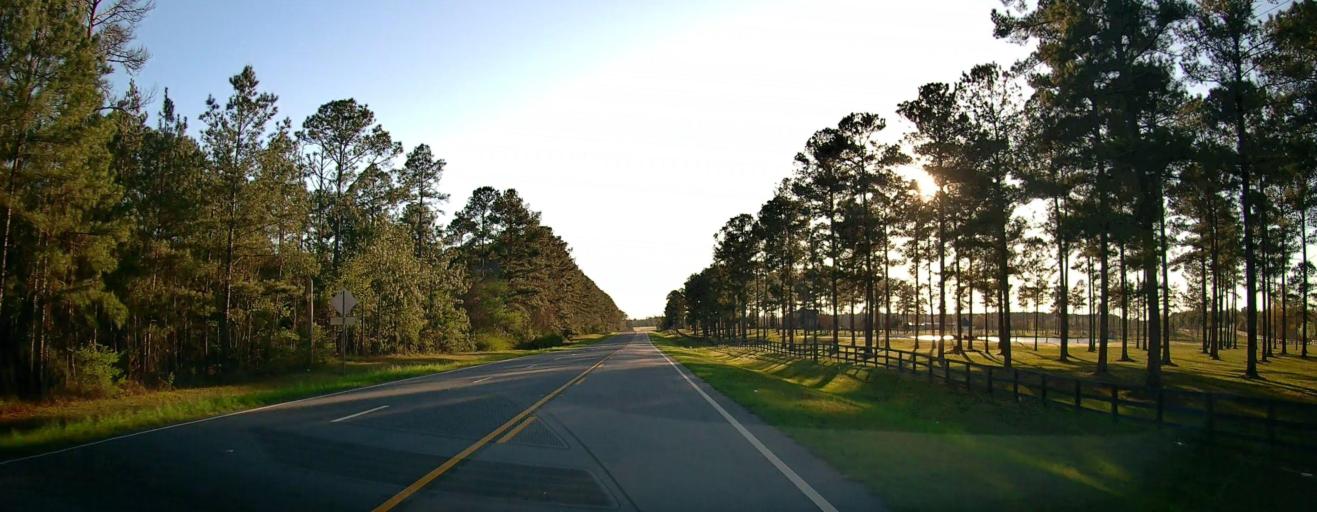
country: US
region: Georgia
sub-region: Wilcox County
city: Abbeville
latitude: 31.9770
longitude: -83.3603
